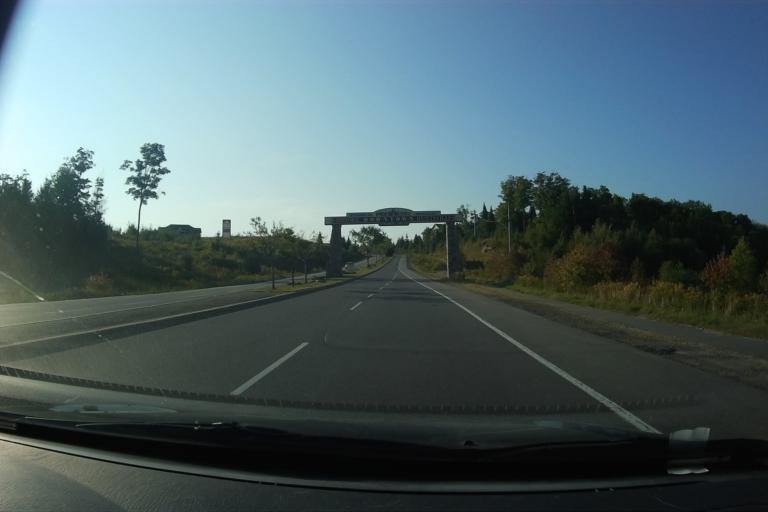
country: CA
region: Ontario
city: Huntsville
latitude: 45.3434
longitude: -79.2254
